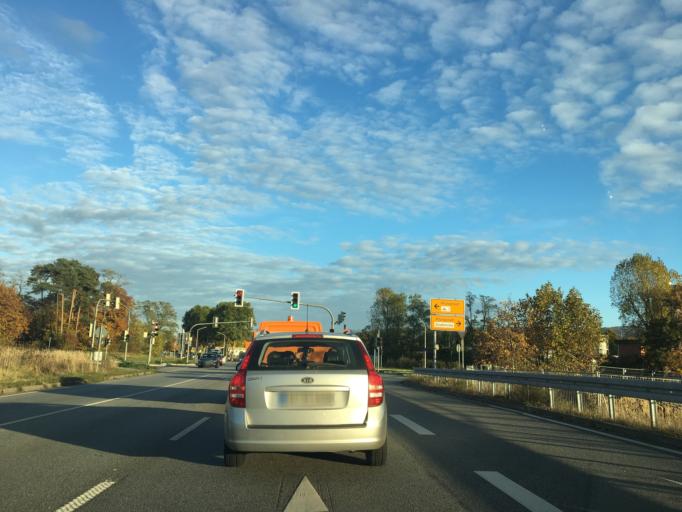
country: DE
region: Hesse
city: Pfungstadt
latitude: 49.8145
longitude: 8.6195
